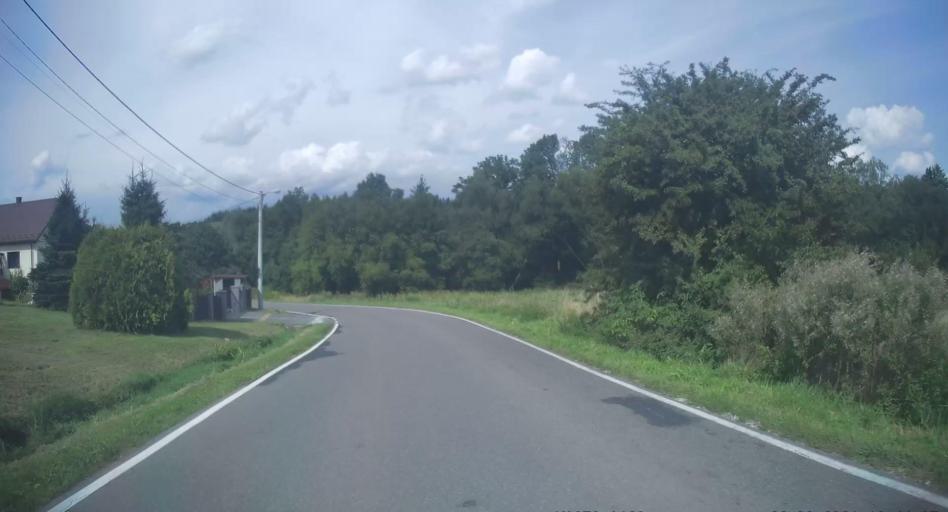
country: PL
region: Lesser Poland Voivodeship
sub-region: Powiat wielicki
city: Pawlikowice
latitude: 49.9501
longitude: 20.0425
